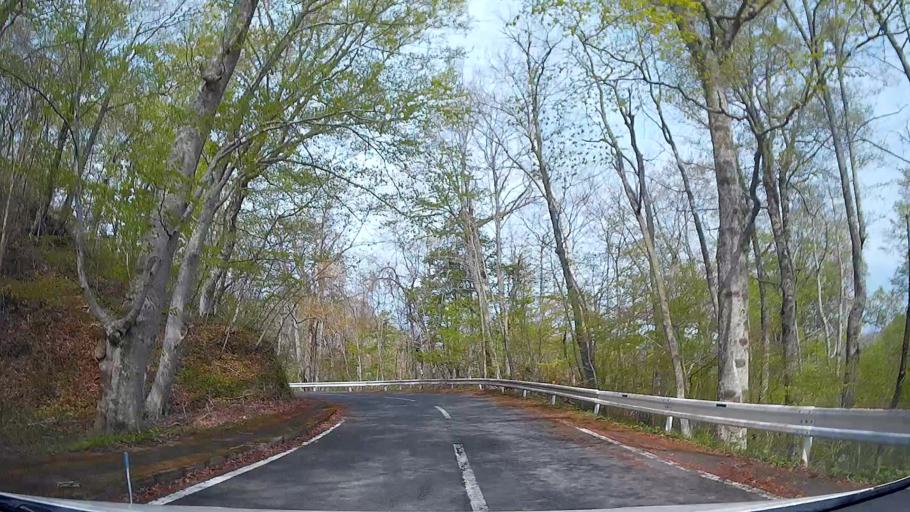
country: JP
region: Akita
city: Hanawa
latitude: 40.4385
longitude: 140.9171
